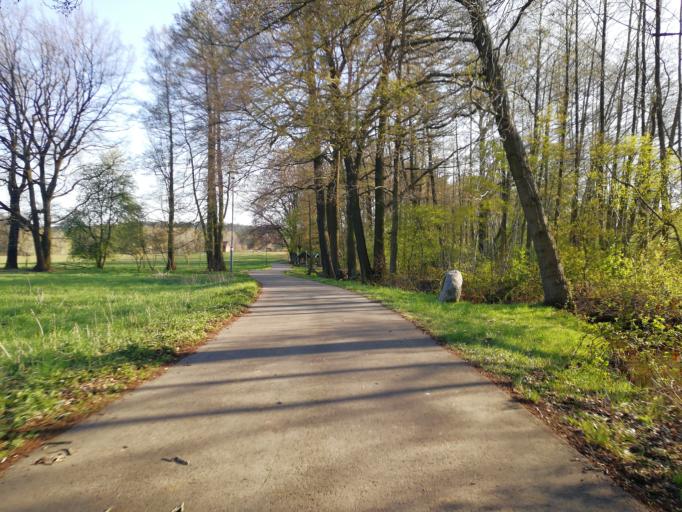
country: DE
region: Brandenburg
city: Calau
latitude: 51.7220
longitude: 13.9544
